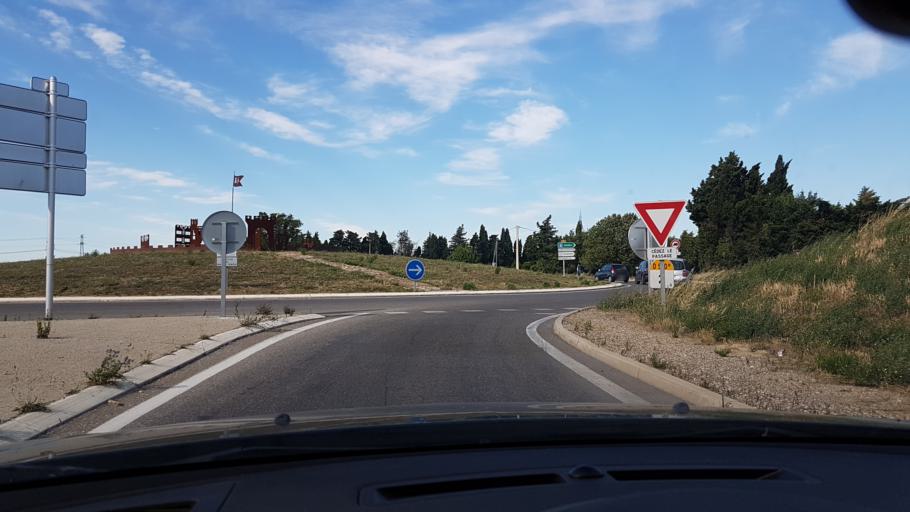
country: FR
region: Provence-Alpes-Cote d'Azur
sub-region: Departement des Bouches-du-Rhone
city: Rognonas
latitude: 43.9081
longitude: 4.7906
